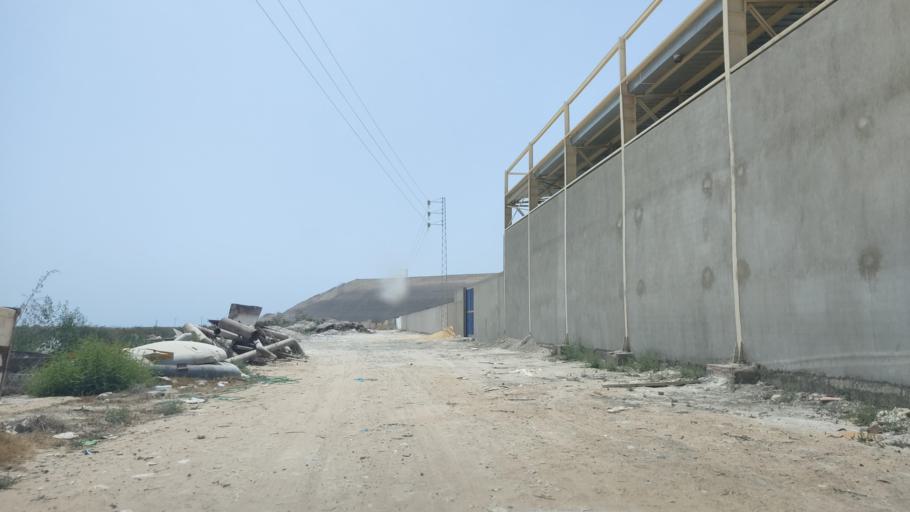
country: TN
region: Safaqis
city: Sfax
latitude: 34.7059
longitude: 10.7269
